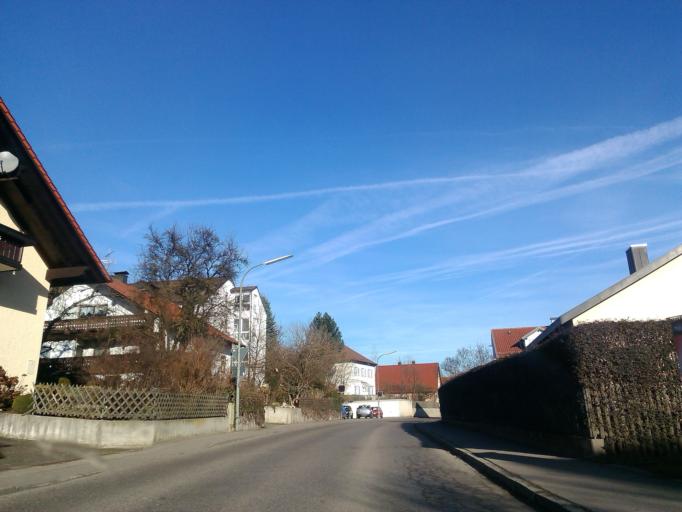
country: DE
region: Bavaria
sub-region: Swabia
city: Aichach
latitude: 48.4687
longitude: 11.1256
